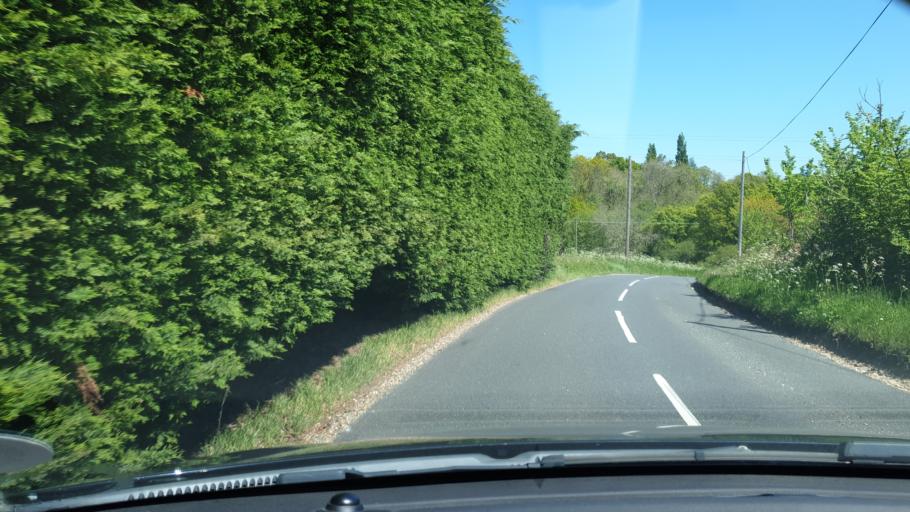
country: GB
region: England
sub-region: Essex
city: Little Clacton
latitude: 51.8653
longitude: 1.1210
